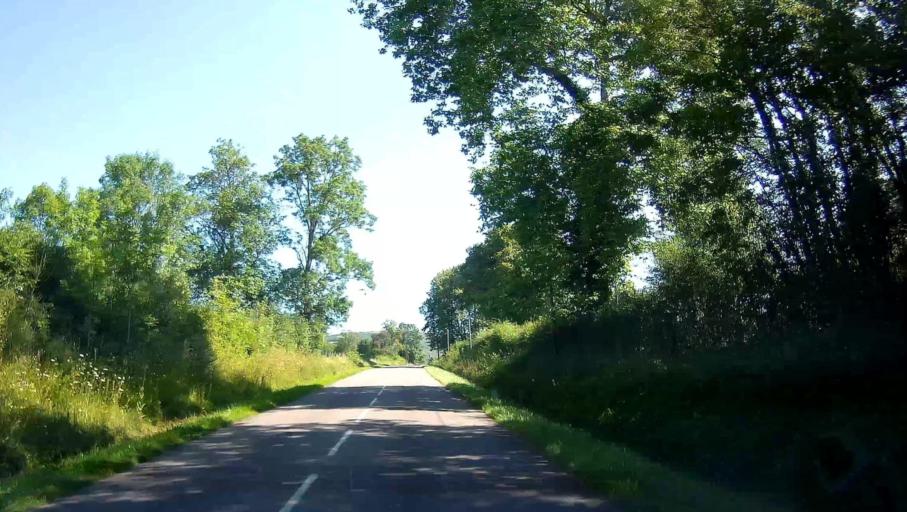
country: FR
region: Bourgogne
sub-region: Departement de la Cote-d'Or
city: Nolay
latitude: 46.9118
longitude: 4.5976
